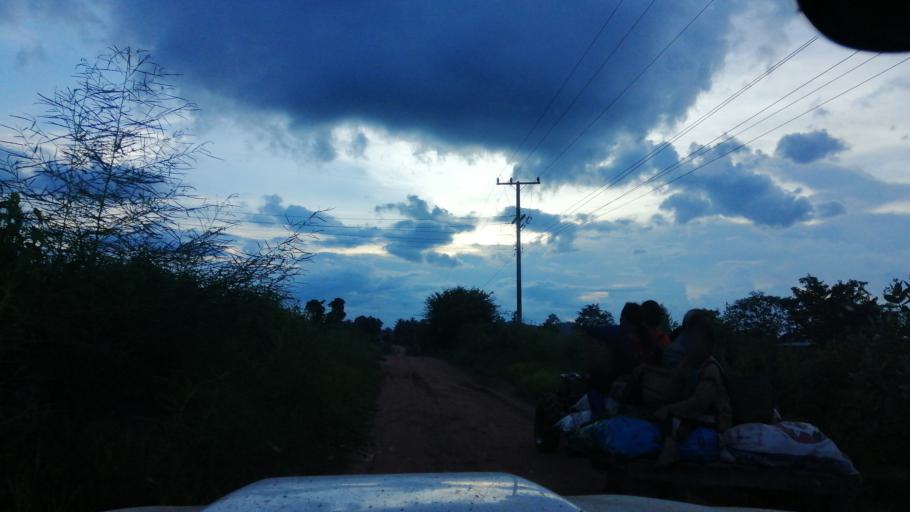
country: TH
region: Uttaradit
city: Ban Khok
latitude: 17.8779
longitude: 101.0531
